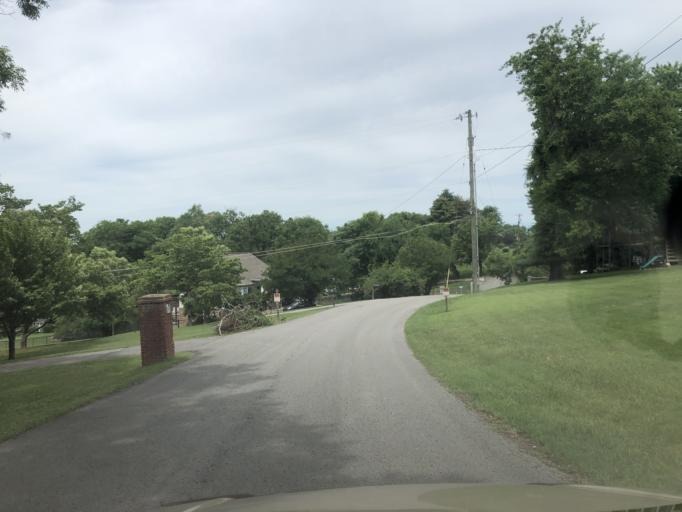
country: US
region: Tennessee
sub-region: Davidson County
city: Lakewood
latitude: 36.2519
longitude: -86.6180
